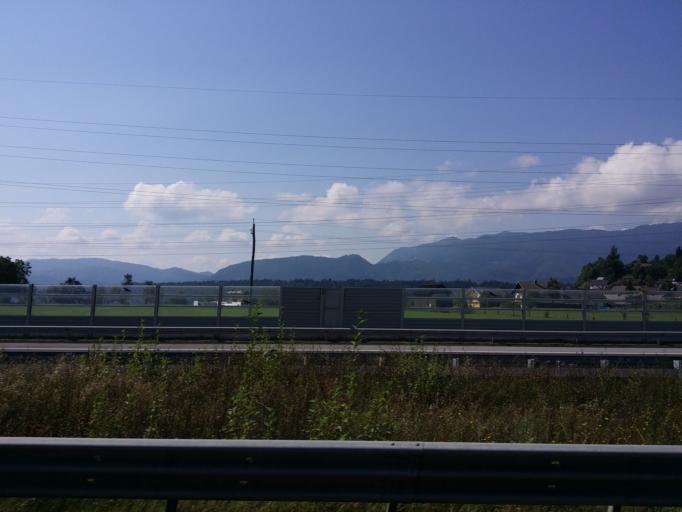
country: SI
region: Trzic
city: Bistrica pri Trzicu
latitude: 46.3153
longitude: 14.2512
